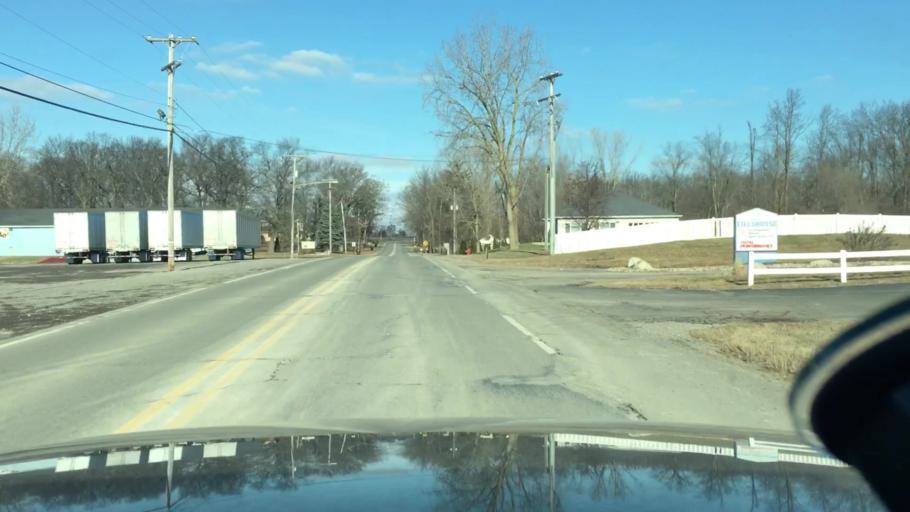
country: US
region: Michigan
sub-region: Jackson County
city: Jackson
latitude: 42.2847
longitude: -84.4308
